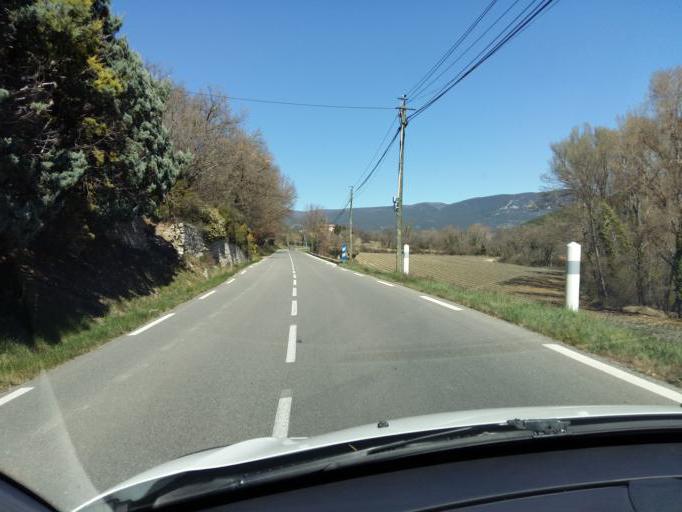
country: FR
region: Provence-Alpes-Cote d'Azur
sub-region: Departement du Vaucluse
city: Saignon
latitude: 43.8891
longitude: 5.4273
